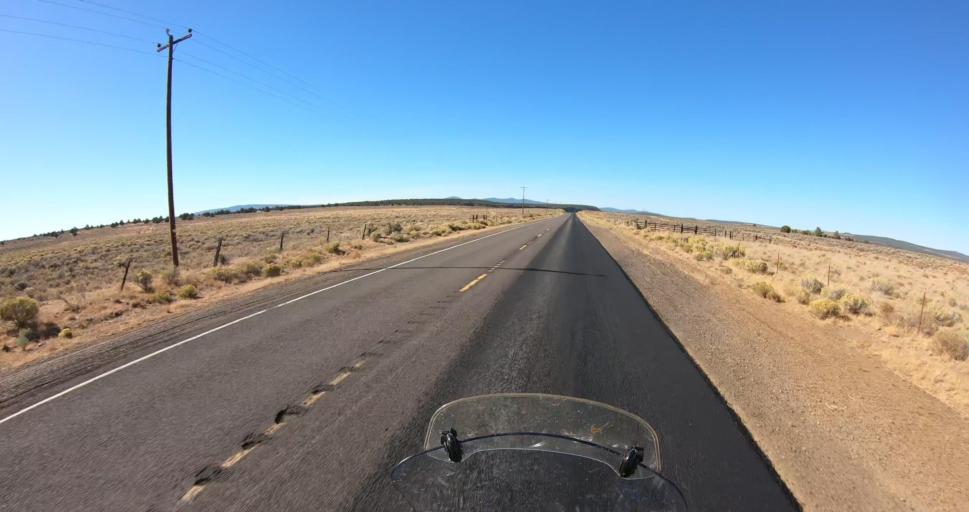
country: US
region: Oregon
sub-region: Deschutes County
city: La Pine
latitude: 43.1388
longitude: -121.0797
